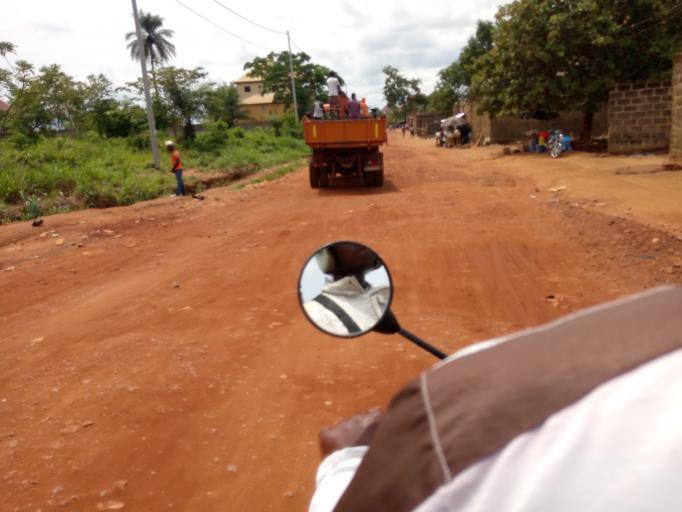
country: SL
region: Western Area
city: Waterloo
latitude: 8.3590
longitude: -13.0789
